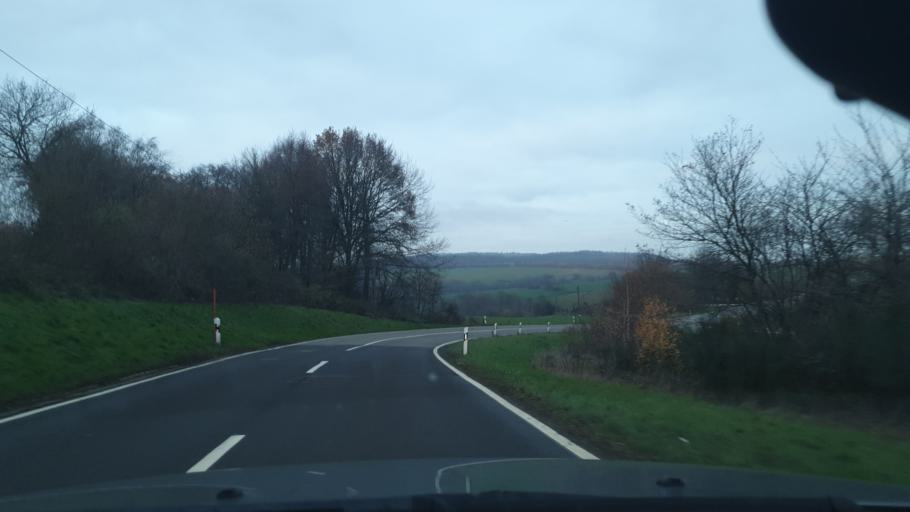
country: DE
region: Rheinland-Pfalz
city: Langwieden
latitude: 49.3669
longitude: 7.5050
